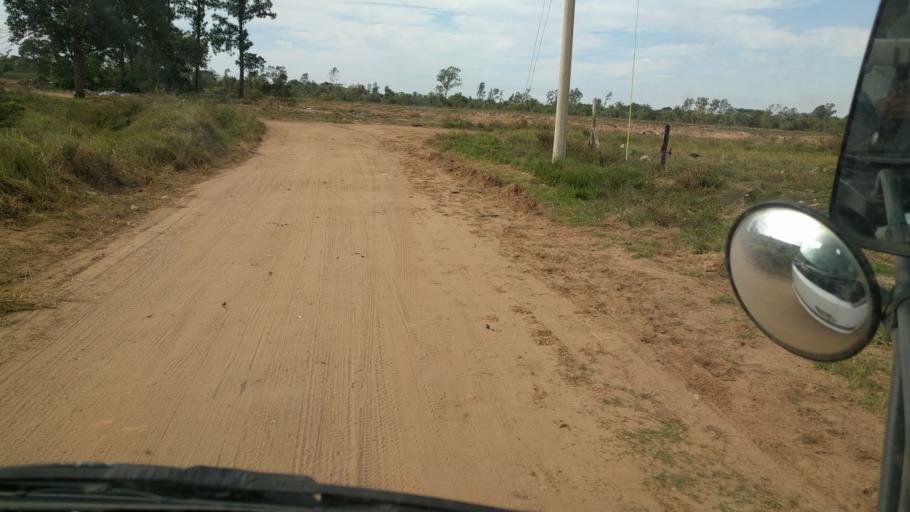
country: BO
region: Santa Cruz
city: Santa Cruz de la Sierra
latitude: -17.6823
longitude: -63.1430
